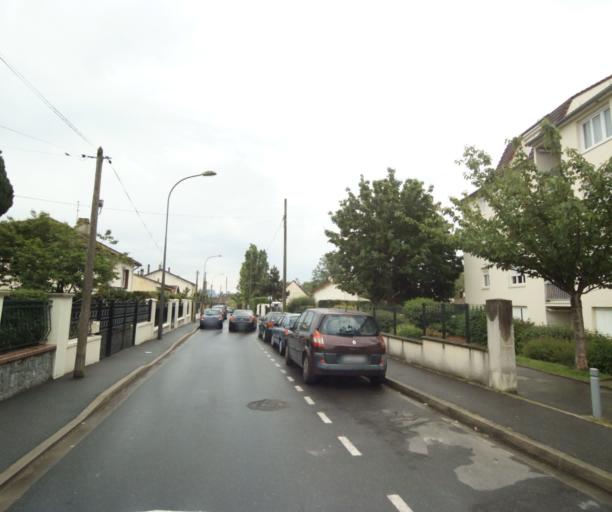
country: FR
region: Ile-de-France
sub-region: Departement du Val-d'Oise
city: Bezons
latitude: 48.9476
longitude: 2.2228
